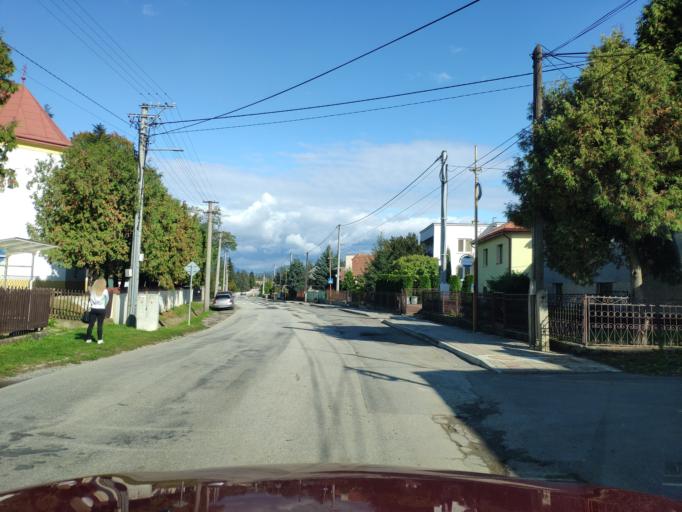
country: SK
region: Presovsky
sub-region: Okres Presov
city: Presov
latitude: 48.9170
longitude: 21.2608
